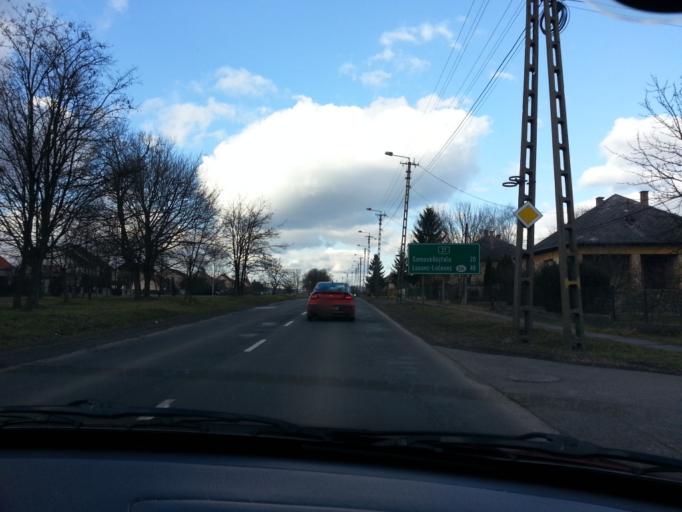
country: HU
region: Nograd
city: Batonyterenye
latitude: 48.0159
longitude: 19.8221
